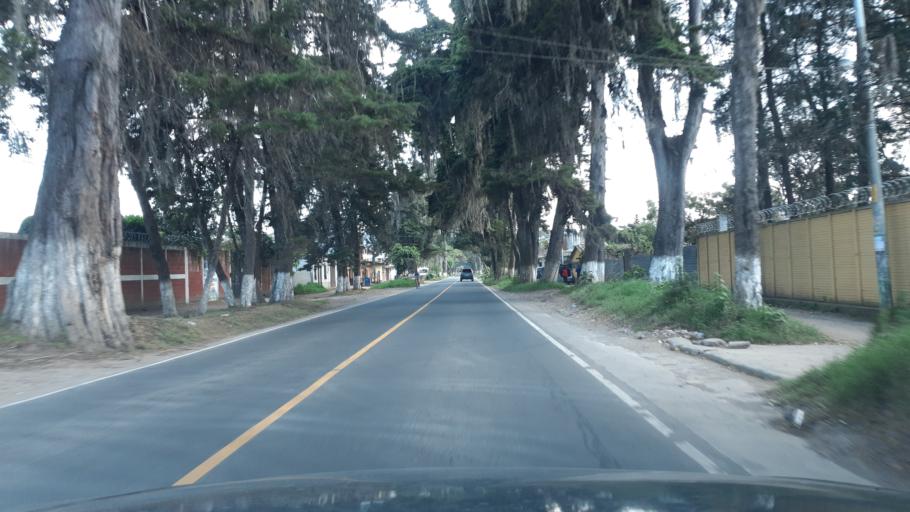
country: GT
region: Chimaltenango
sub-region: Municipio de Chimaltenango
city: Chimaltenango
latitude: 14.6457
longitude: -90.8116
